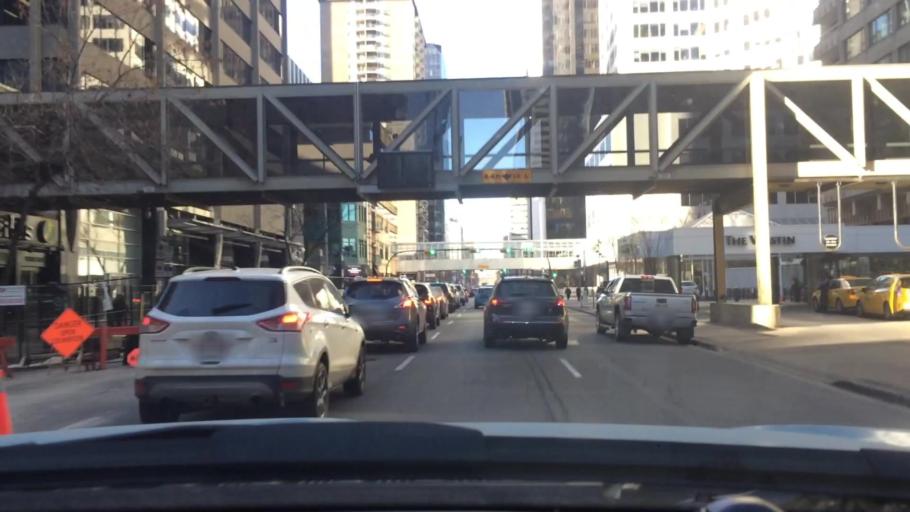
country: CA
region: Alberta
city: Calgary
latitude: 51.0495
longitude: -114.0689
